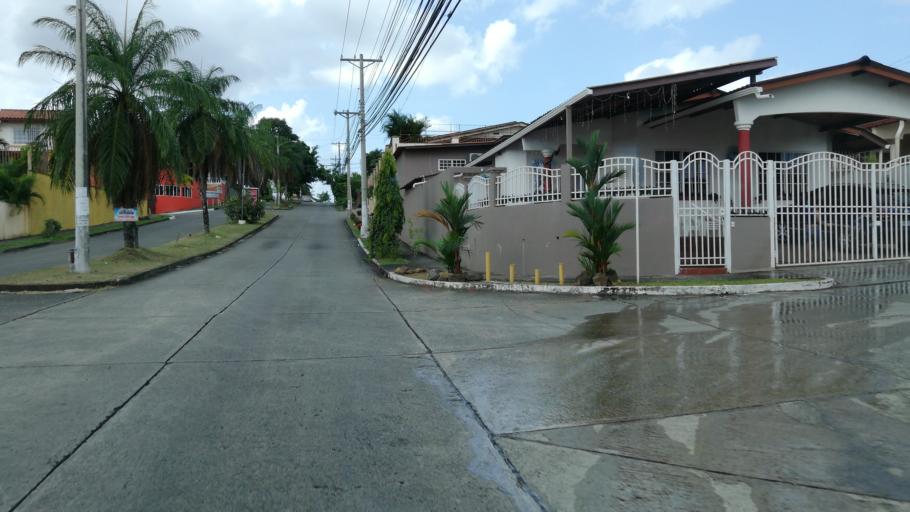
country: PA
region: Panama
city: San Miguelito
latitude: 9.0653
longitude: -79.4562
